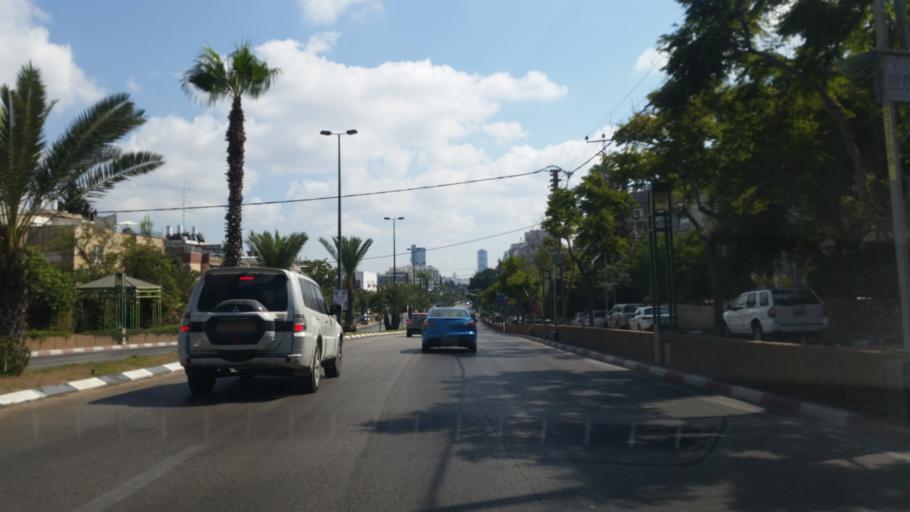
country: IL
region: Tel Aviv
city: Ramat HaSharon
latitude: 32.1206
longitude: 34.8252
